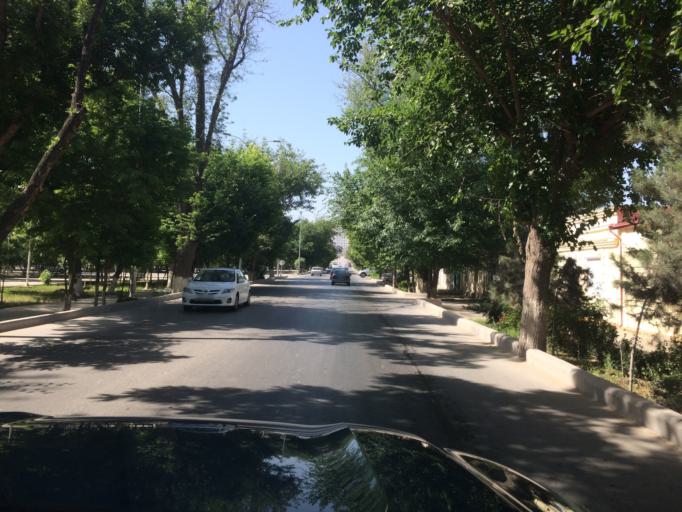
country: TM
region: Ahal
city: Ashgabat
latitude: 37.9480
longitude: 58.3612
